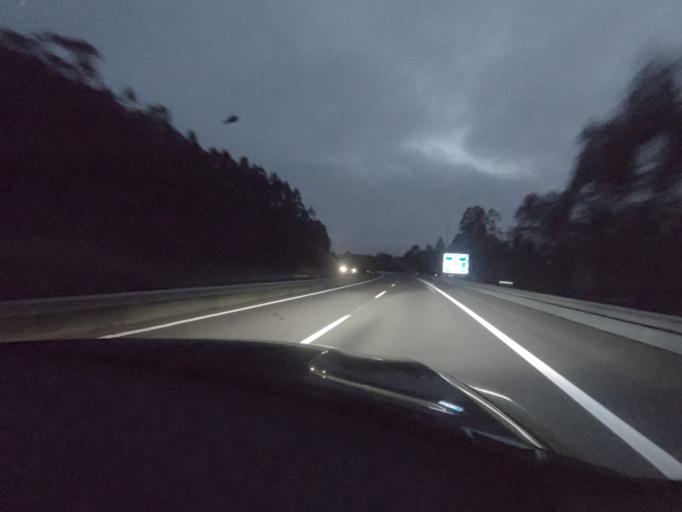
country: PT
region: Leiria
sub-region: Leiria
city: Caranguejeira
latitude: 39.7902
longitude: -8.7368
